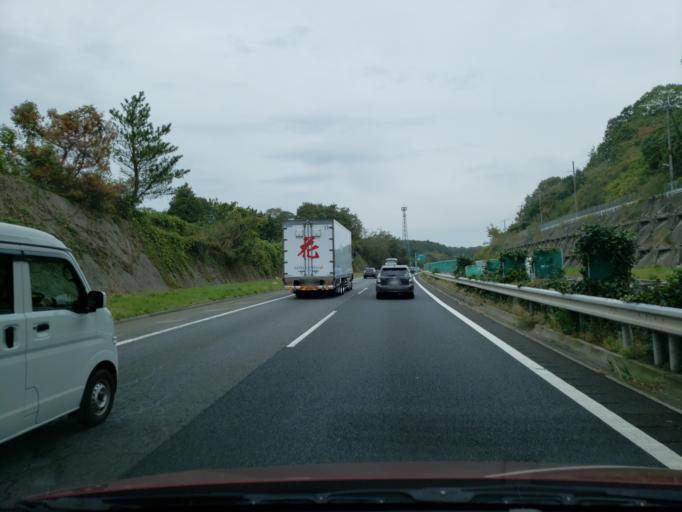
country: JP
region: Hyogo
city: Sandacho
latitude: 34.8355
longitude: 135.1894
